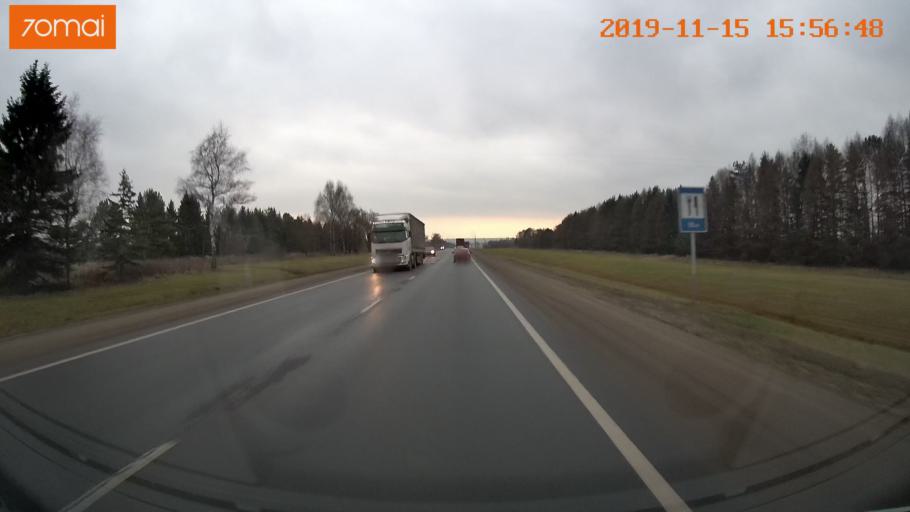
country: RU
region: Jaroslavl
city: Yaroslavl
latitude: 57.8378
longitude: 39.9697
